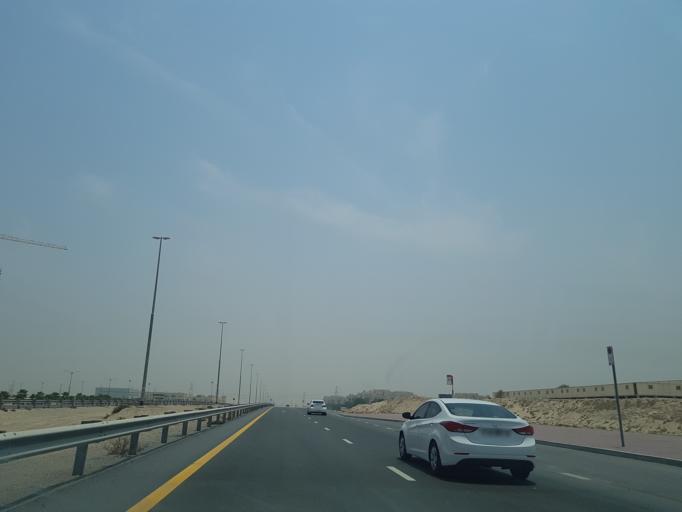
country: AE
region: Dubai
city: Dubai
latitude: 25.0139
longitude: 55.2491
